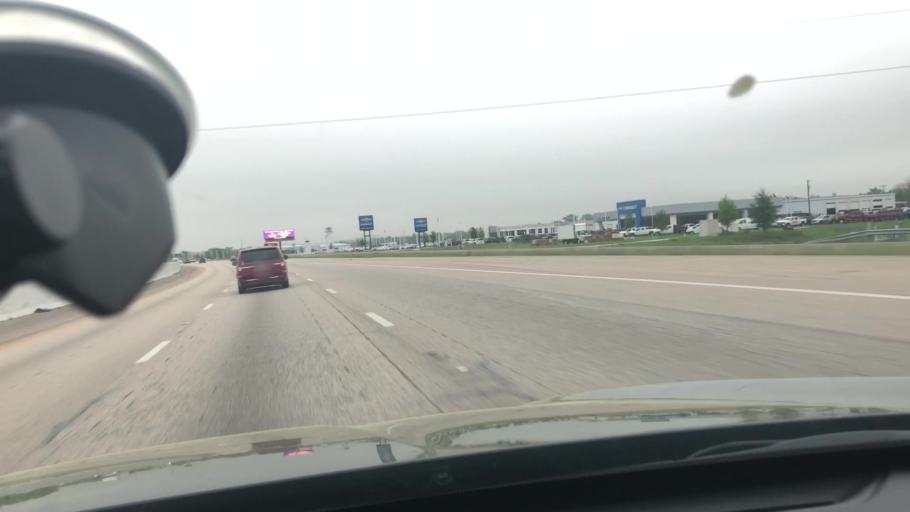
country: US
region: Texas
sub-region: Bell County
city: Belton
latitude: 31.0590
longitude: -97.4397
